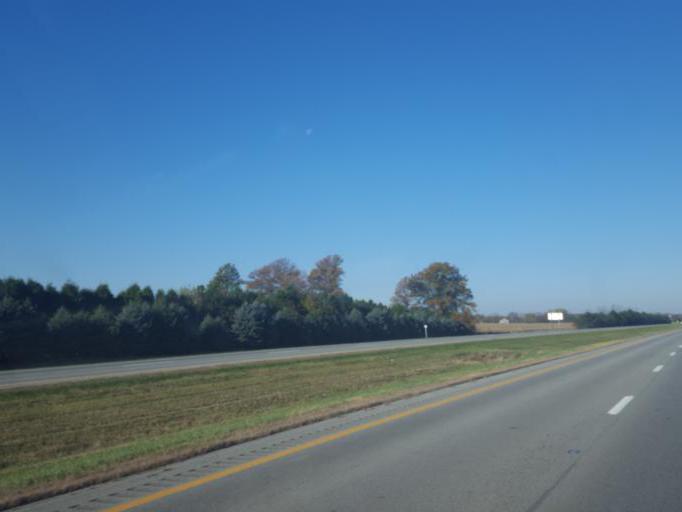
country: US
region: Ohio
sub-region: Wyandot County
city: Upper Sandusky
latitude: 40.7322
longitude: -83.1998
